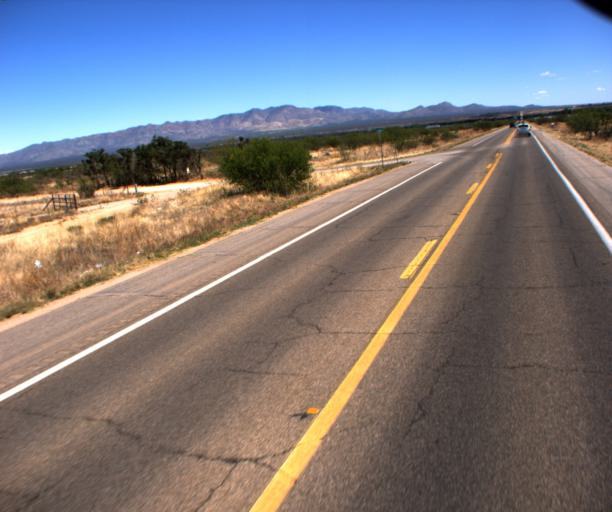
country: US
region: Arizona
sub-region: Cochise County
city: Sierra Vista Southeast
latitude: 31.3799
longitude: -110.1400
